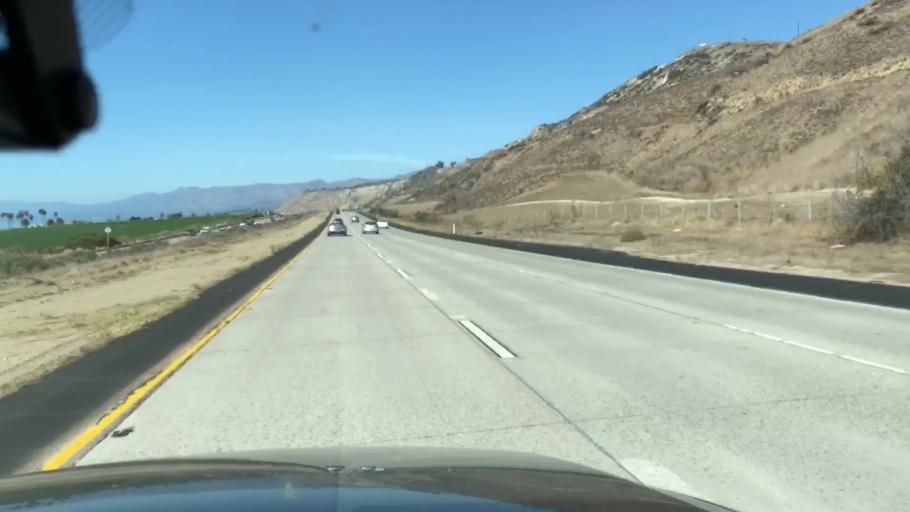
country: US
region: California
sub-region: Ventura County
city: Oak View
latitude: 34.3350
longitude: -119.4029
